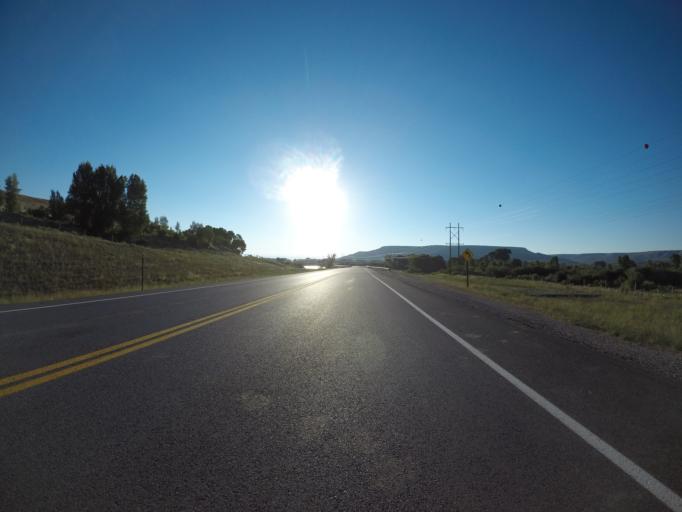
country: US
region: Wyoming
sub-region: Sublette County
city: Marbleton
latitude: 42.5700
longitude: -109.9528
